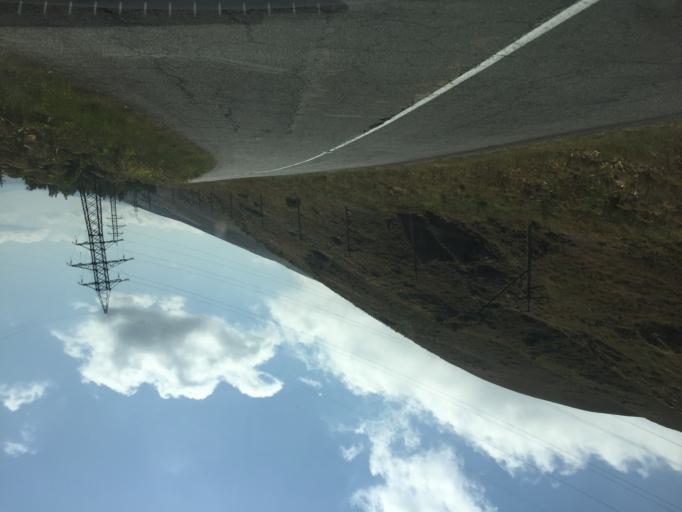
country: AM
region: Geghark'unik'i Marz
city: Tsovagyugh
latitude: 40.6325
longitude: 44.9863
